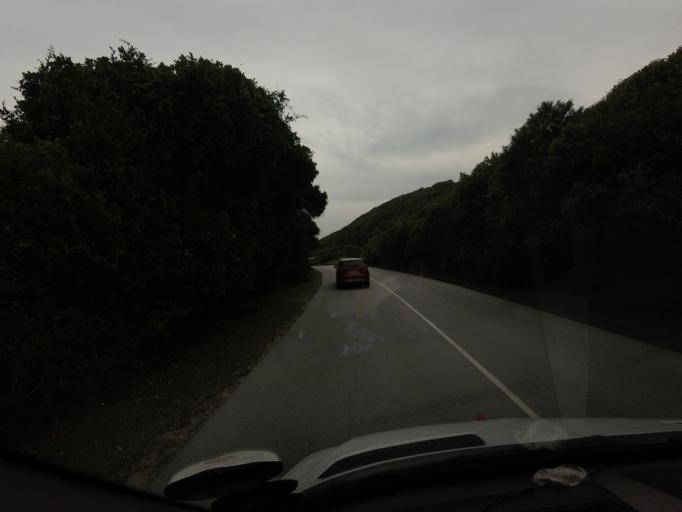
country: ZA
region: Eastern Cape
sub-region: Cacadu District Municipality
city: Kareedouw
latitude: -34.0230
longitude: 23.8897
